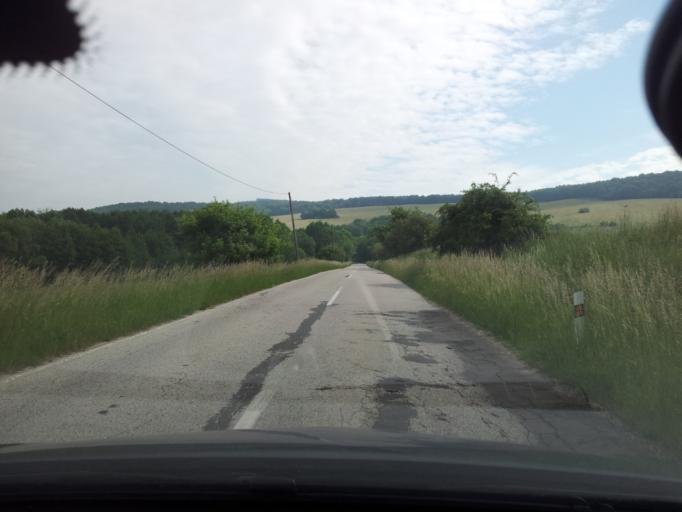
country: SK
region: Nitriansky
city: Zlate Moravce
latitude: 48.5022
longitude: 18.4295
